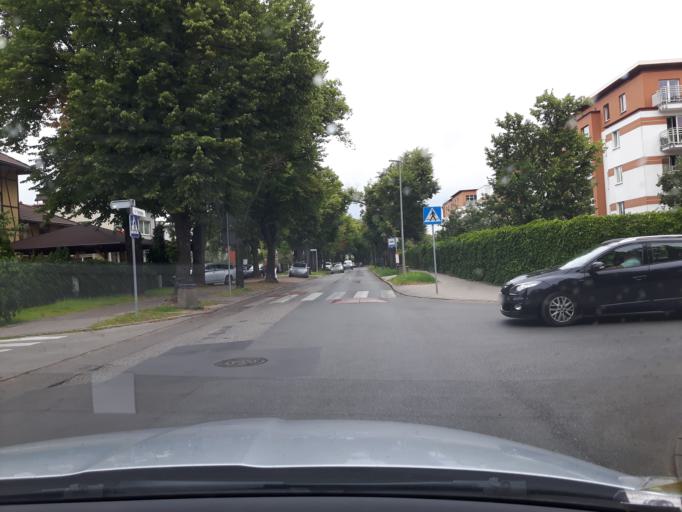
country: PL
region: Pomeranian Voivodeship
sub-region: Sopot
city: Sopot
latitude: 54.4143
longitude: 18.5796
